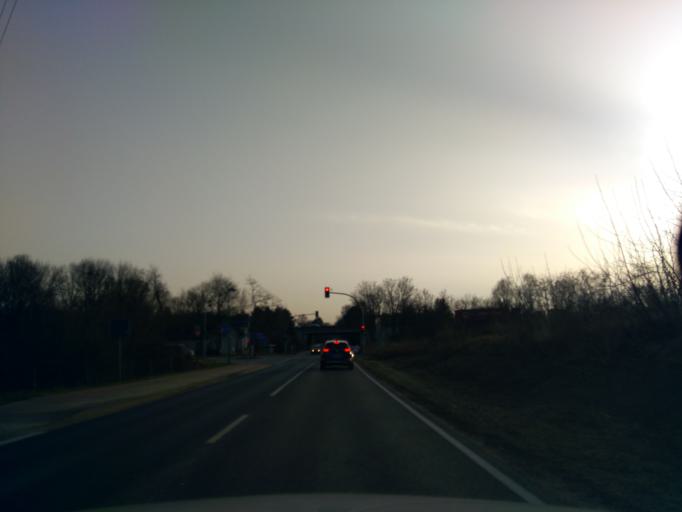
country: DE
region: Berlin
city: Blankenfelde
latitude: 52.6824
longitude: 13.3739
